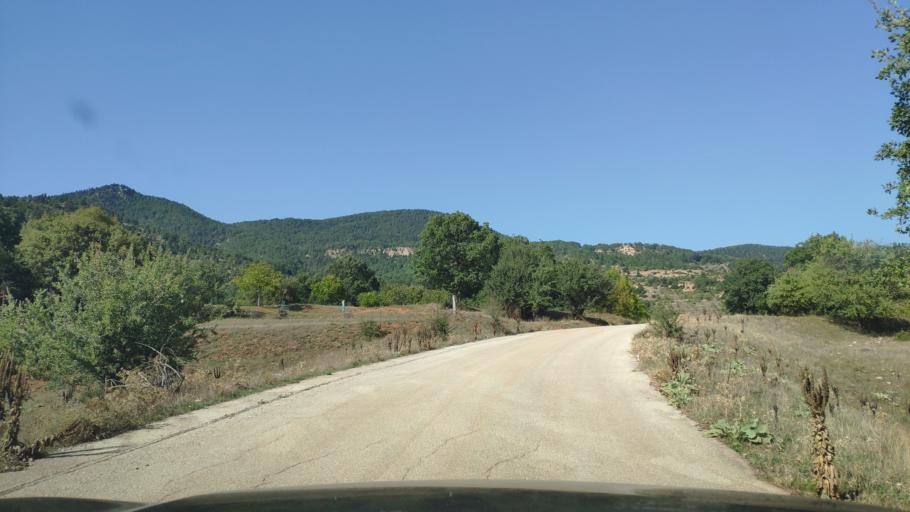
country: GR
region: West Greece
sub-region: Nomos Achaias
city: Aiyira
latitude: 37.9912
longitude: 22.3567
